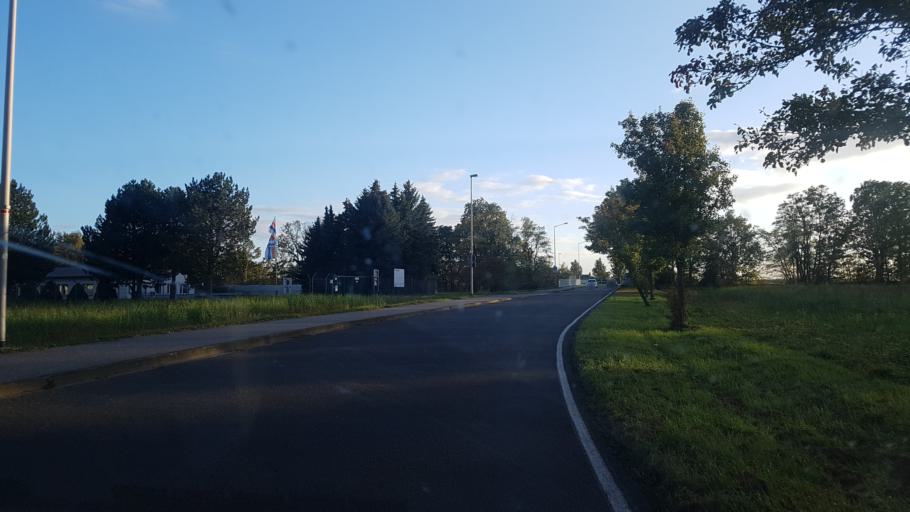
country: DE
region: Saxony
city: Oschatz
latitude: 51.3156
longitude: 13.0913
